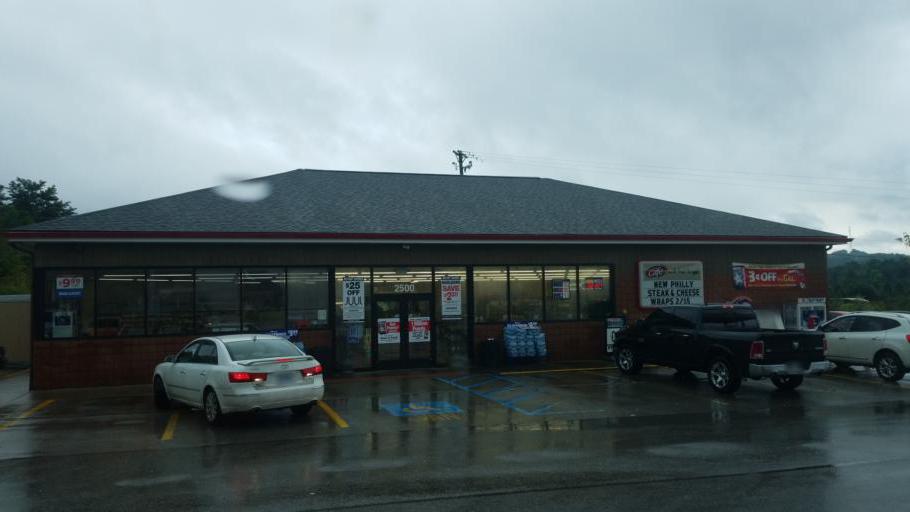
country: US
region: Kentucky
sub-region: Rowan County
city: Morehead
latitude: 38.2014
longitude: -83.4753
